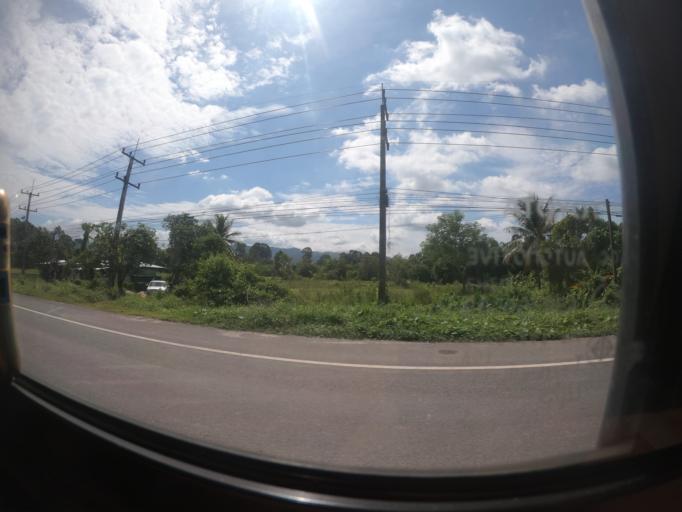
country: TH
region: Nakhon Nayok
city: Nakhon Nayok
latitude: 14.2758
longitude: 101.2930
